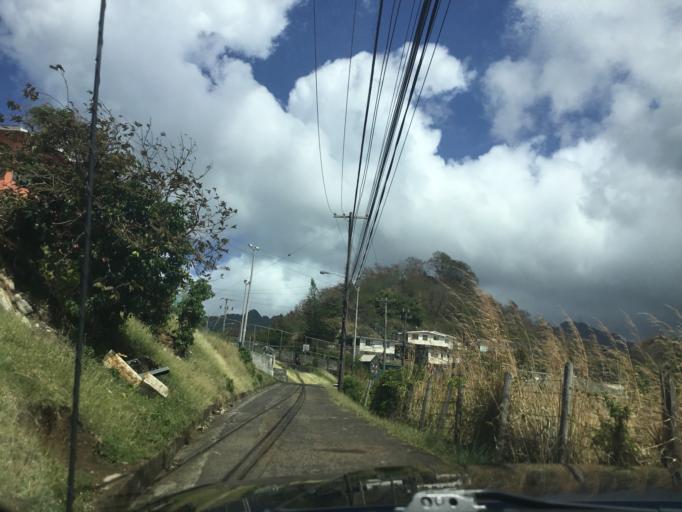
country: VC
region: Saint George
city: Kingstown Park
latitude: 13.1597
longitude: -61.2388
